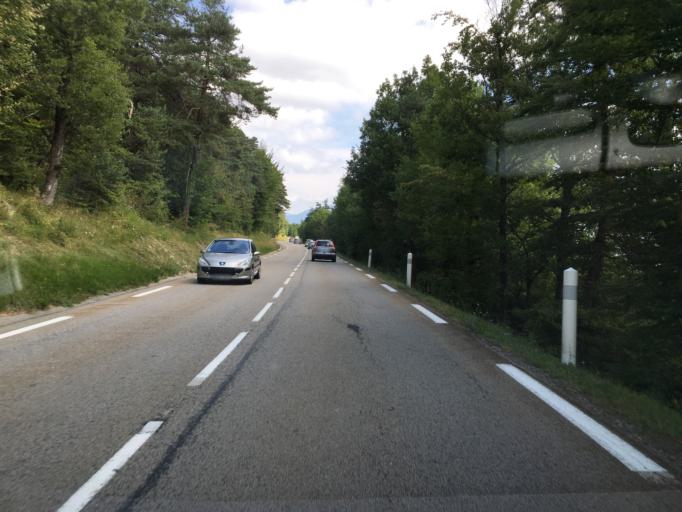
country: FR
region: Rhone-Alpes
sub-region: Departement de l'Isere
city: Mens
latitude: 44.7801
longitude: 5.6456
